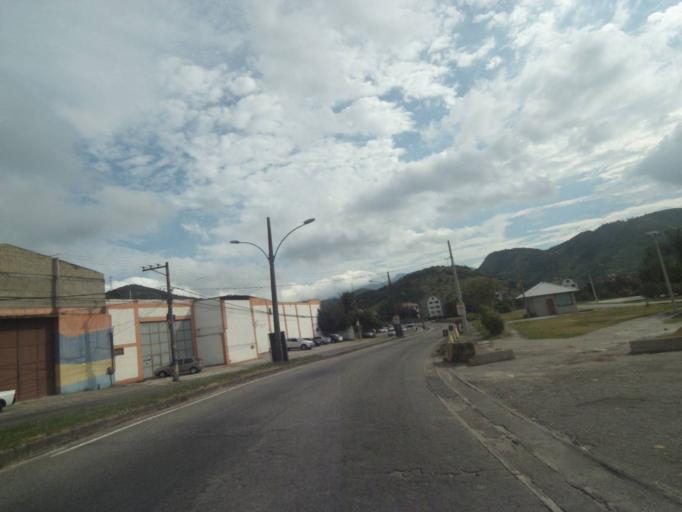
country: BR
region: Rio de Janeiro
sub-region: Nilopolis
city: Nilopolis
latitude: -22.8933
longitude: -43.3956
